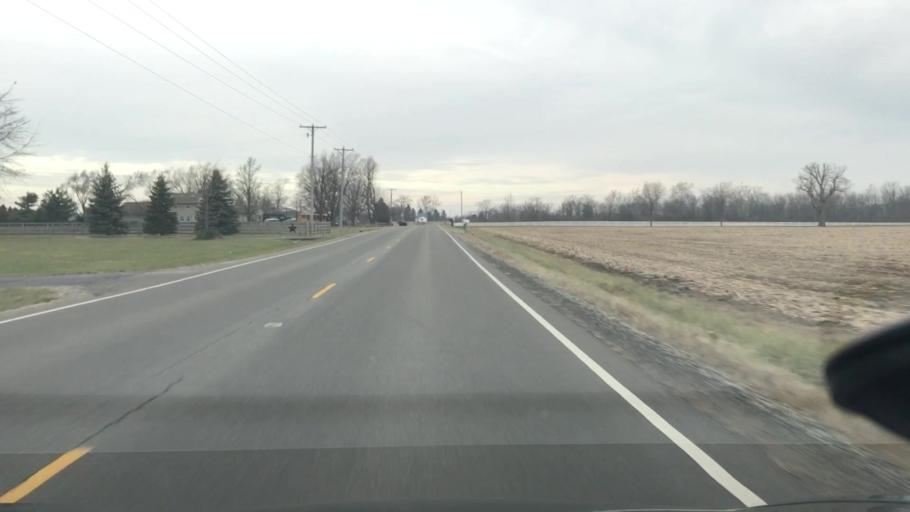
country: US
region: Ohio
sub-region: Madison County
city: Mount Sterling
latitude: 39.7658
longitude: -83.3115
